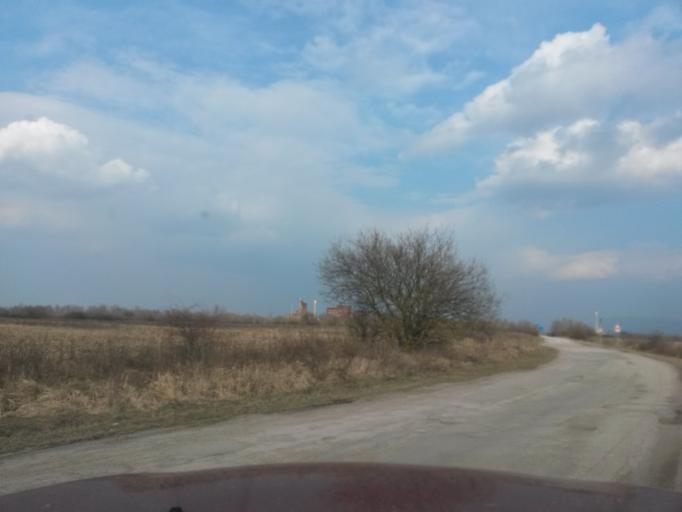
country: HU
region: Borsod-Abauj-Zemplen
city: Gonc
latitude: 48.5757
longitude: 21.2009
